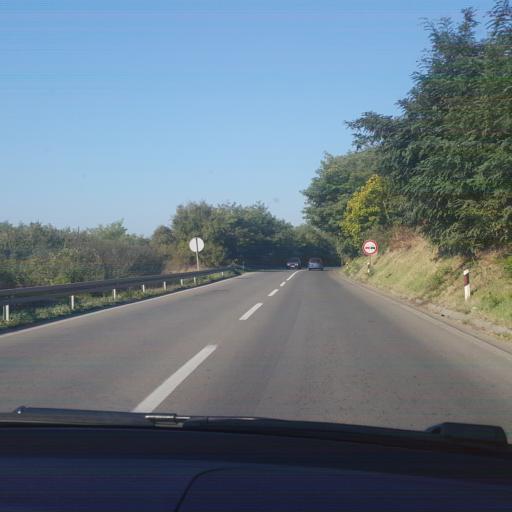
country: RS
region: Central Serbia
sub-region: Toplicki Okrug
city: Prokuplje
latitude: 43.2331
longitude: 21.5326
